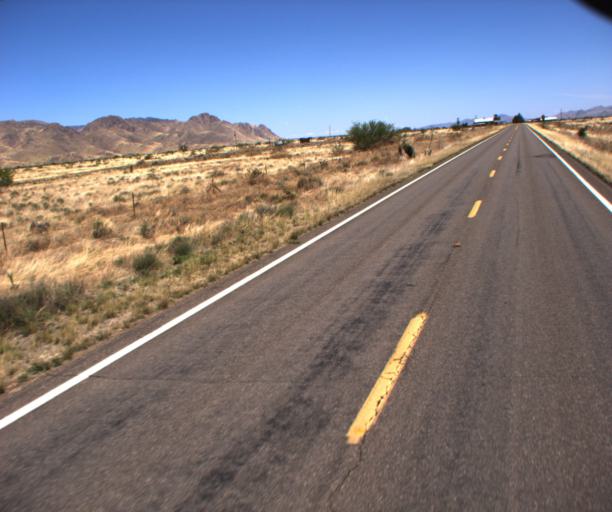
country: US
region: Arizona
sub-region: Cochise County
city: Douglas
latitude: 31.6880
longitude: -109.1342
